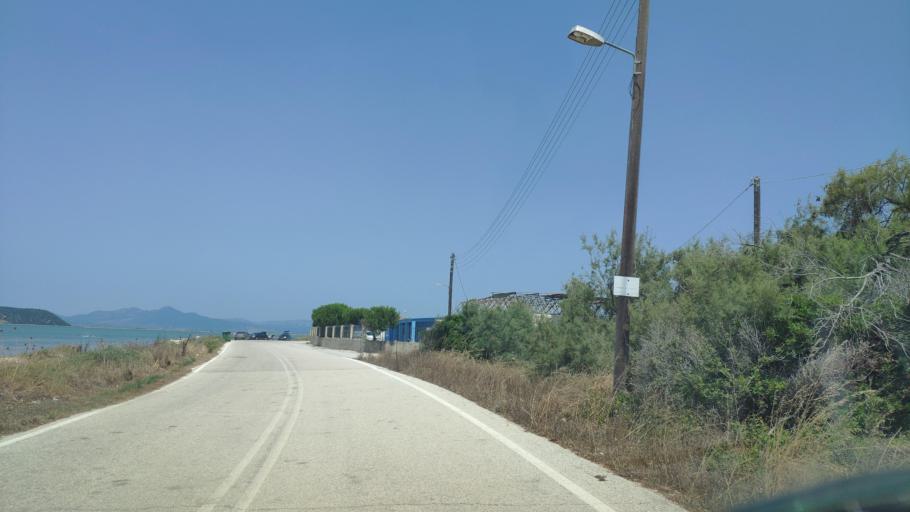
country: GR
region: Epirus
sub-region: Nomos Artas
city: Aneza
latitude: 39.0195
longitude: 20.9125
